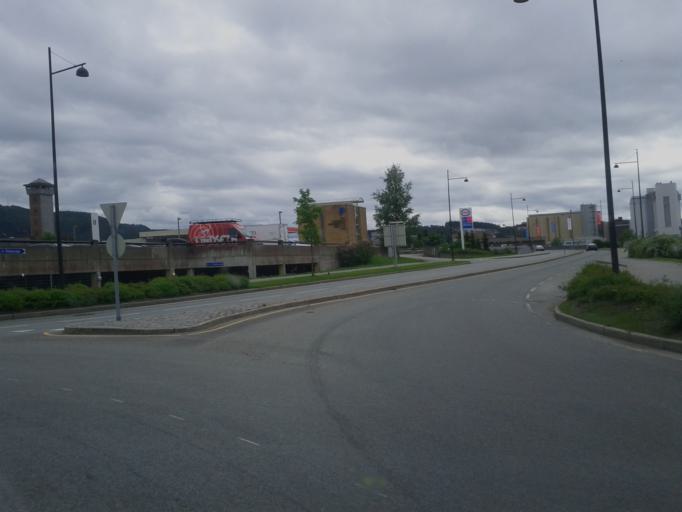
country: NO
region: Nord-Trondelag
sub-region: Steinkjer
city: Steinkjer
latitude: 64.0189
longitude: 11.4905
